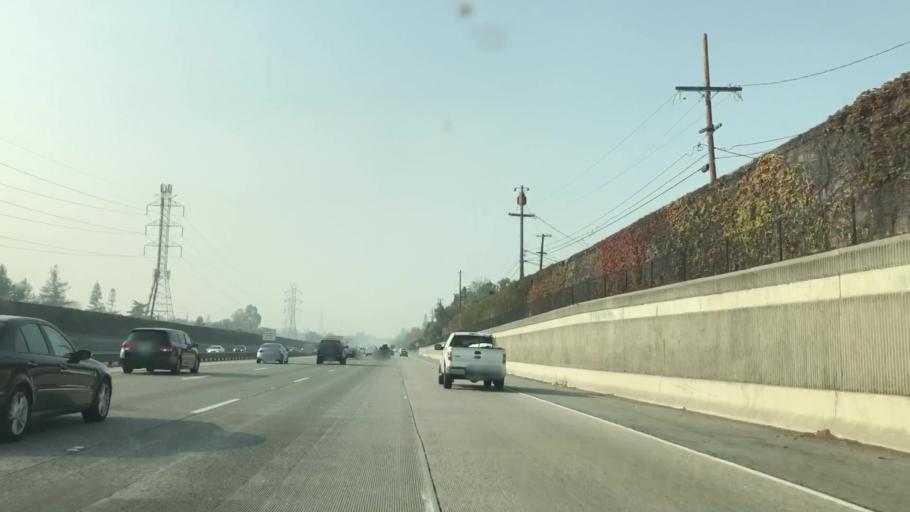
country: US
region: California
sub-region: Santa Clara County
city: Monte Sereno
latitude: 37.2611
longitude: -121.9709
